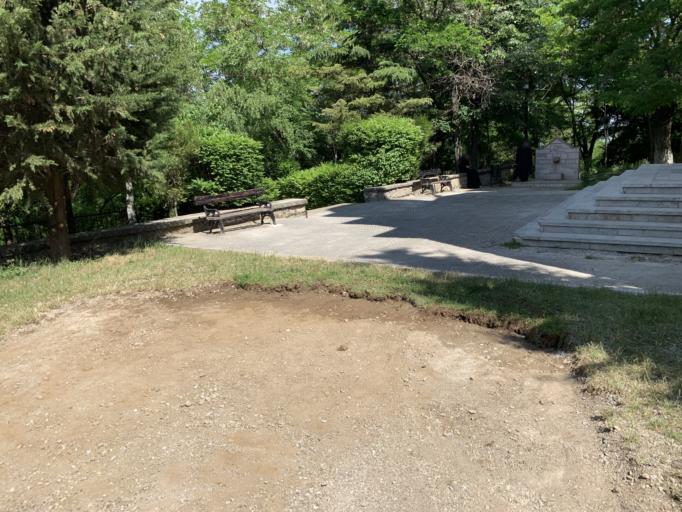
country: AL
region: Korce
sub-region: Rrethi i Korces
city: Korce
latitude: 40.6237
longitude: 20.7864
